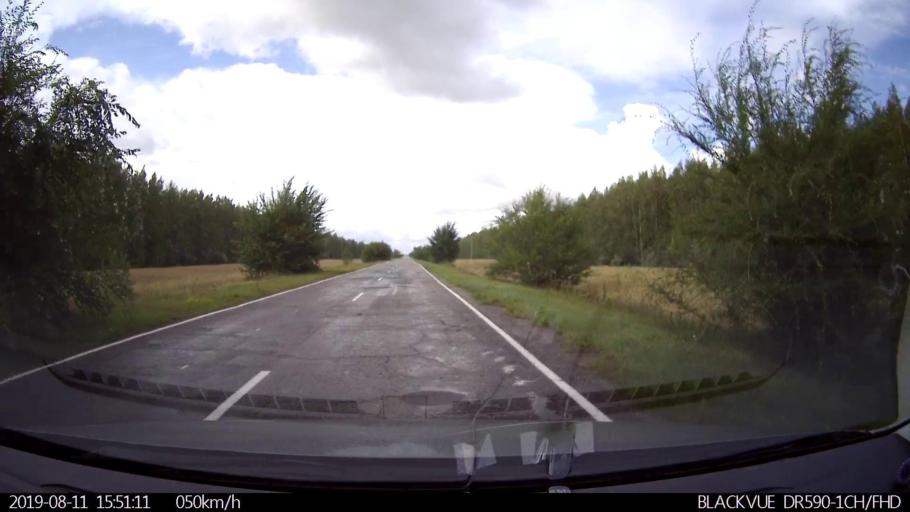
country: RU
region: Ulyanovsk
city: Ignatovka
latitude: 53.9168
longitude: 47.6559
